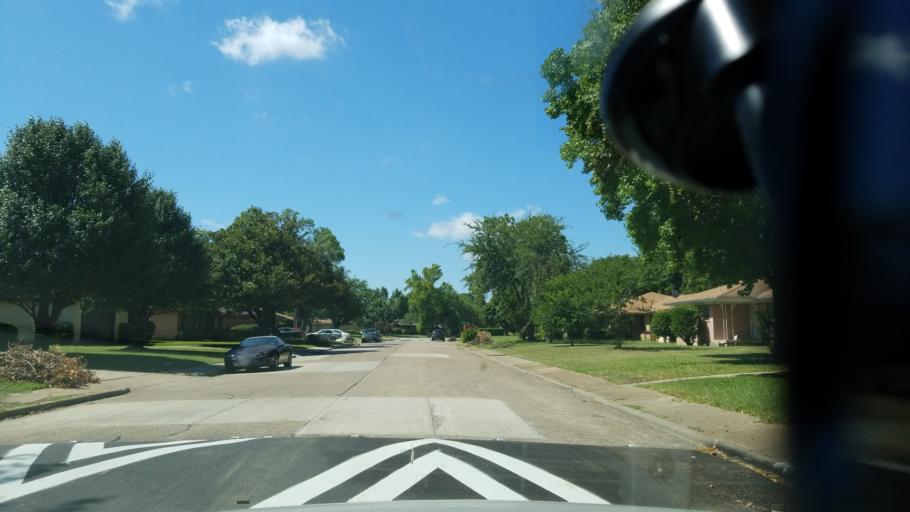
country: US
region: Texas
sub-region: Dallas County
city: Cockrell Hill
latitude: 32.6863
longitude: -96.8280
